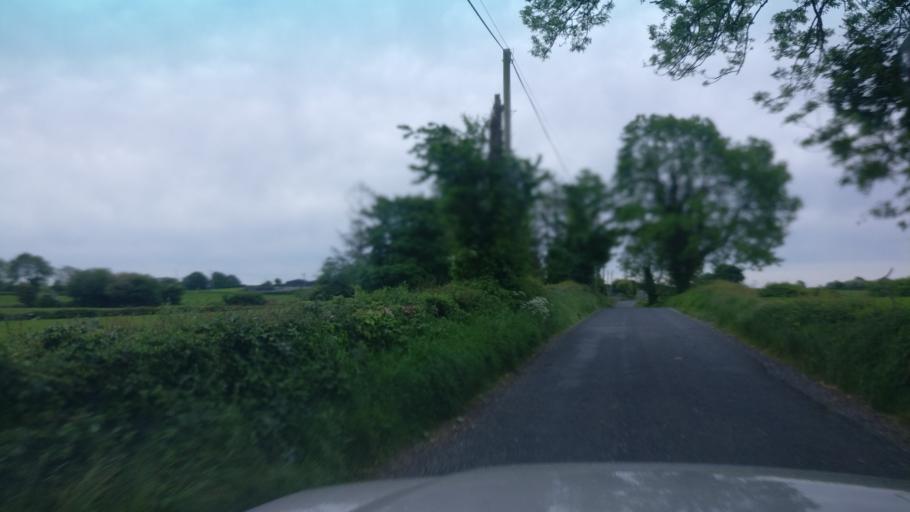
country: IE
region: Connaught
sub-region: County Galway
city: Portumna
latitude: 53.1489
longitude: -8.2915
